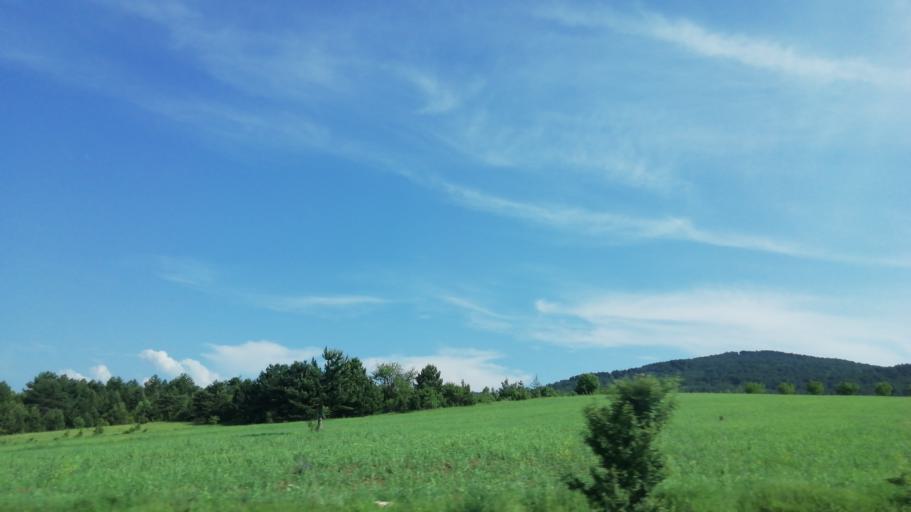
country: TR
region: Karabuk
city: Karabuk
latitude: 41.0922
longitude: 32.5896
